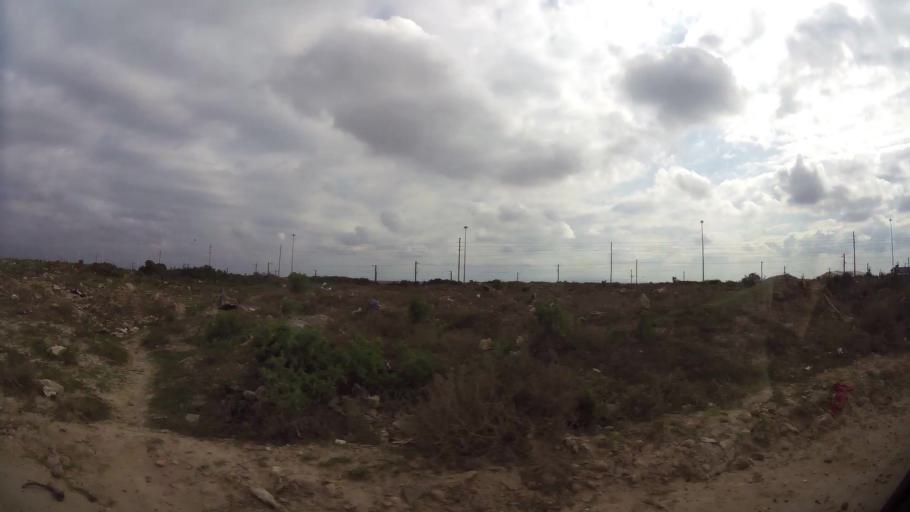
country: ZA
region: Eastern Cape
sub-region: Nelson Mandela Bay Metropolitan Municipality
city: Port Elizabeth
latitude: -33.8247
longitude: 25.6232
